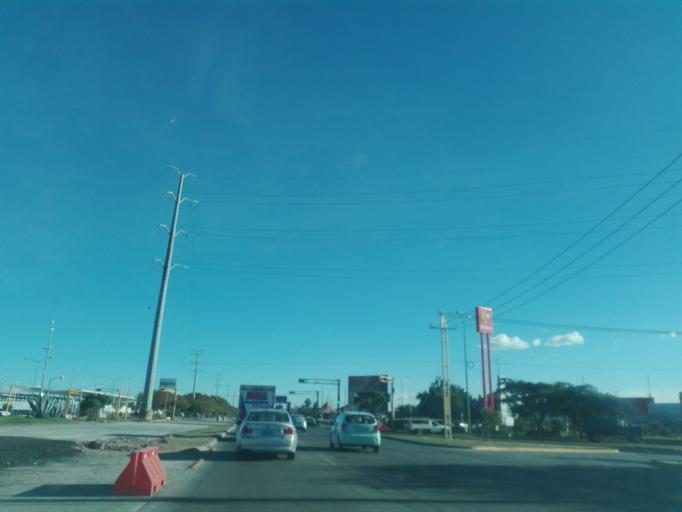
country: MX
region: Guanajuato
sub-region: Leon
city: Medina
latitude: 21.1423
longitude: -101.6332
